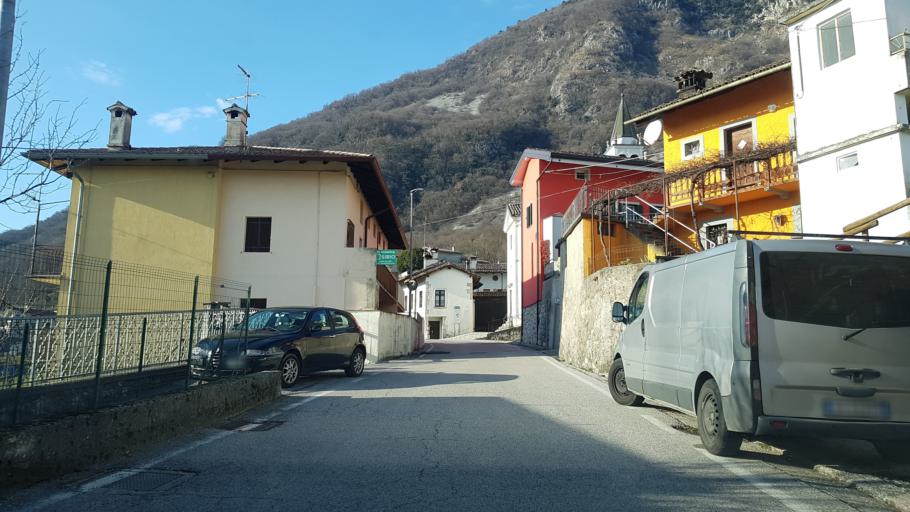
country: IT
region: Friuli Venezia Giulia
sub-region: Provincia di Udine
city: Forgaria nel Friuli
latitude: 46.2258
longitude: 13.0166
